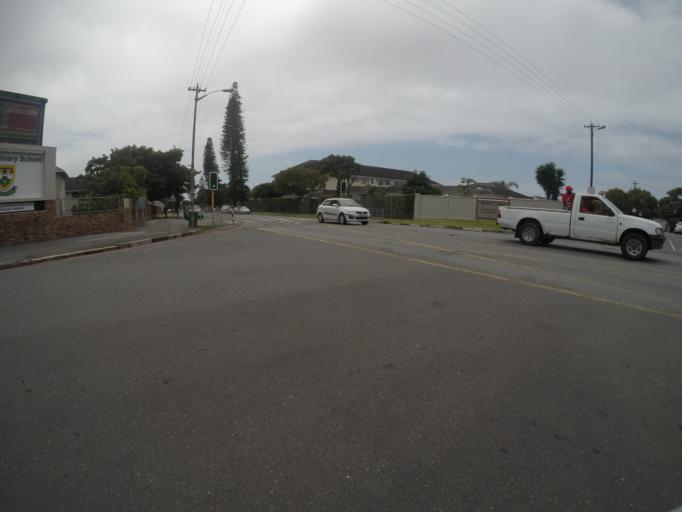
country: ZA
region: Eastern Cape
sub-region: Buffalo City Metropolitan Municipality
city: East London
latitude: -32.9922
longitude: 27.9211
